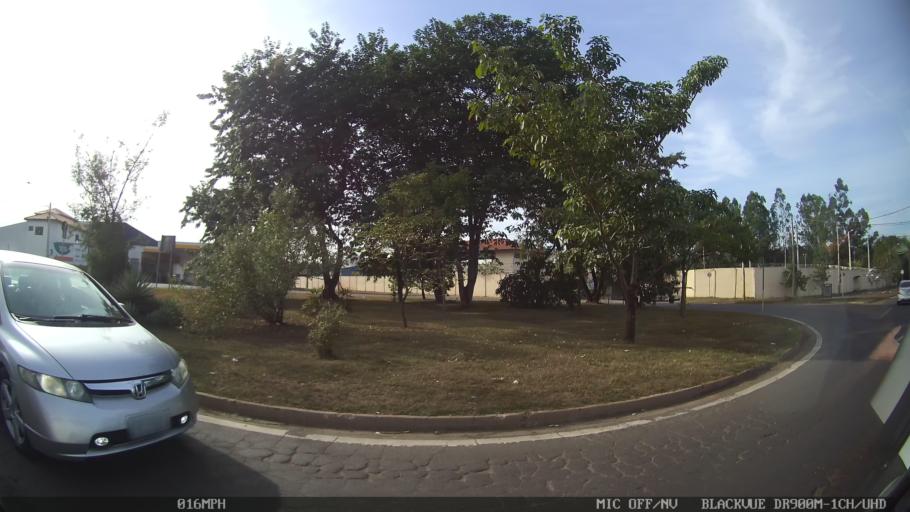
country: BR
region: Sao Paulo
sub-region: Piracicaba
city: Piracicaba
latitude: -22.7000
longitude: -47.6758
